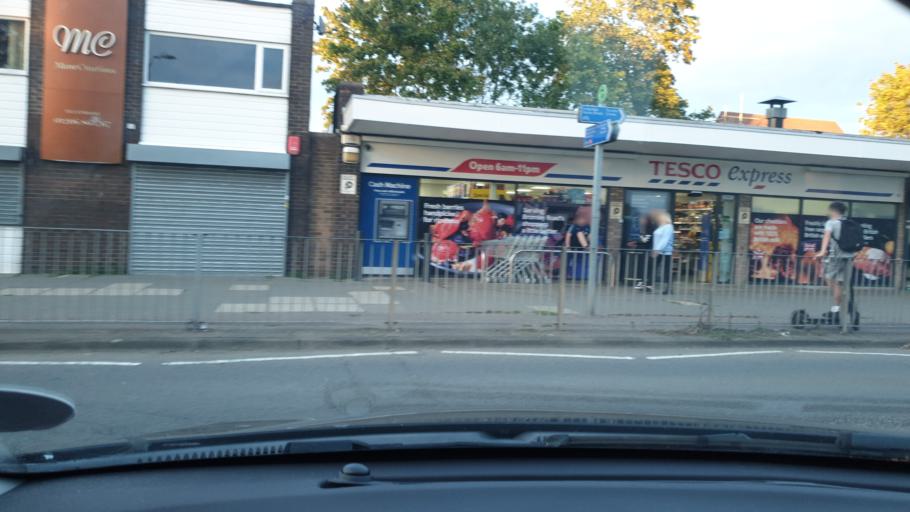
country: GB
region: England
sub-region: Essex
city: Colchester
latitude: 51.8964
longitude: 0.9388
